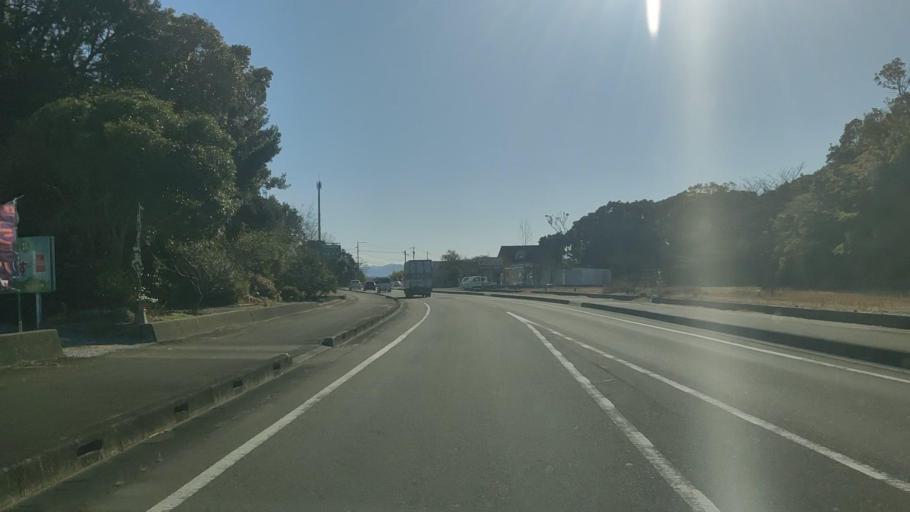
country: JP
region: Miyazaki
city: Miyazaki-shi
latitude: 31.9504
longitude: 131.4601
